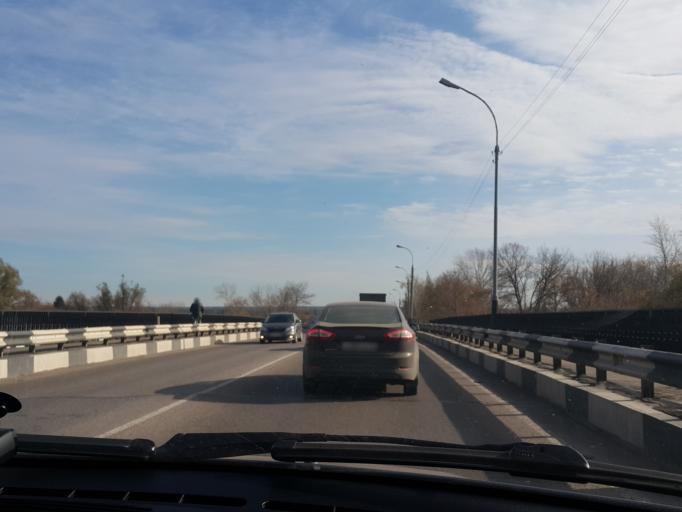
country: RU
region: Tambov
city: Tambov
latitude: 52.7224
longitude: 41.4810
